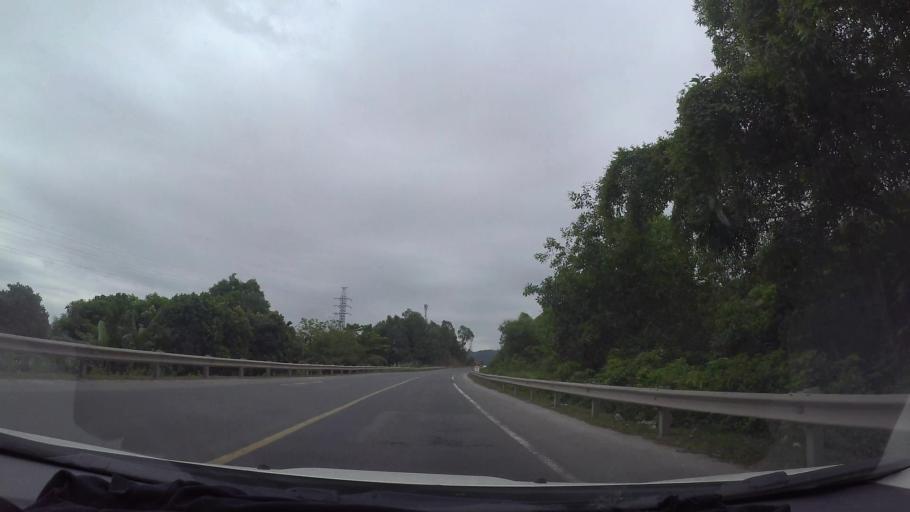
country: VN
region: Da Nang
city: Lien Chieu
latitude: 16.1181
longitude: 108.1038
